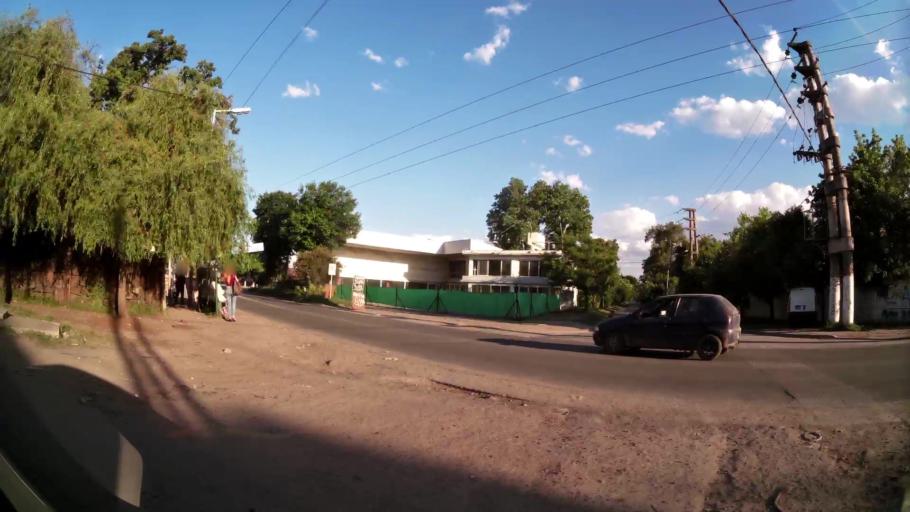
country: AR
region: Buenos Aires
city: Santa Catalina - Dique Lujan
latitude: -34.4672
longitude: -58.7525
